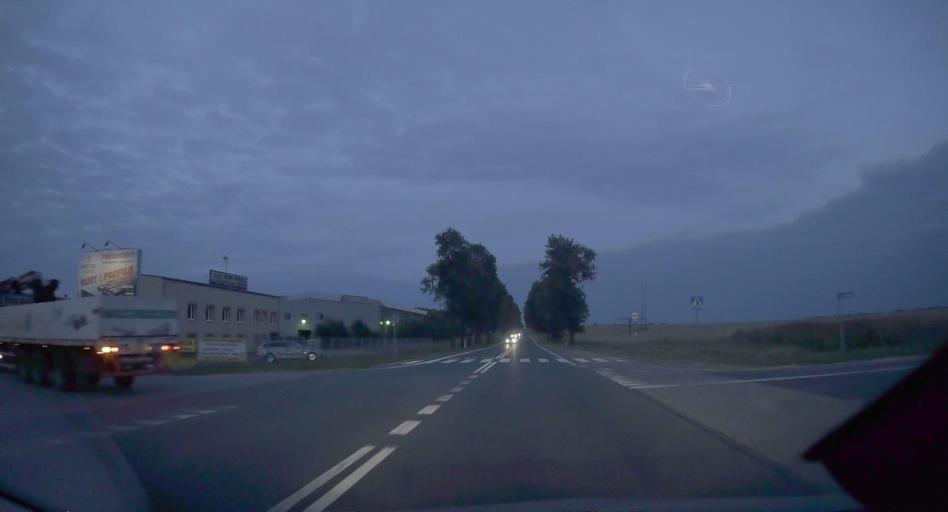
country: PL
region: Silesian Voivodeship
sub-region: Powiat klobucki
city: Klobuck
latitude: 50.9120
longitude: 18.9033
